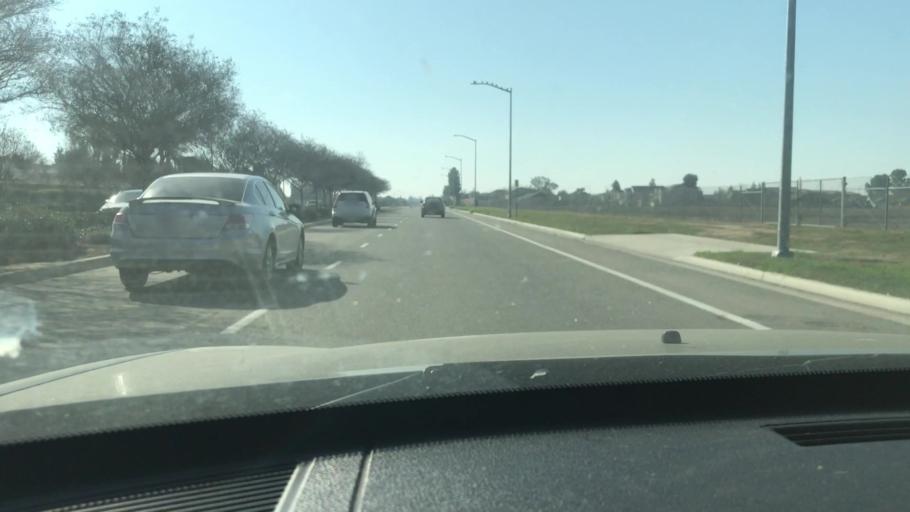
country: US
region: California
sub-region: Fresno County
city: Tarpey Village
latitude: 36.7920
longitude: -119.6641
